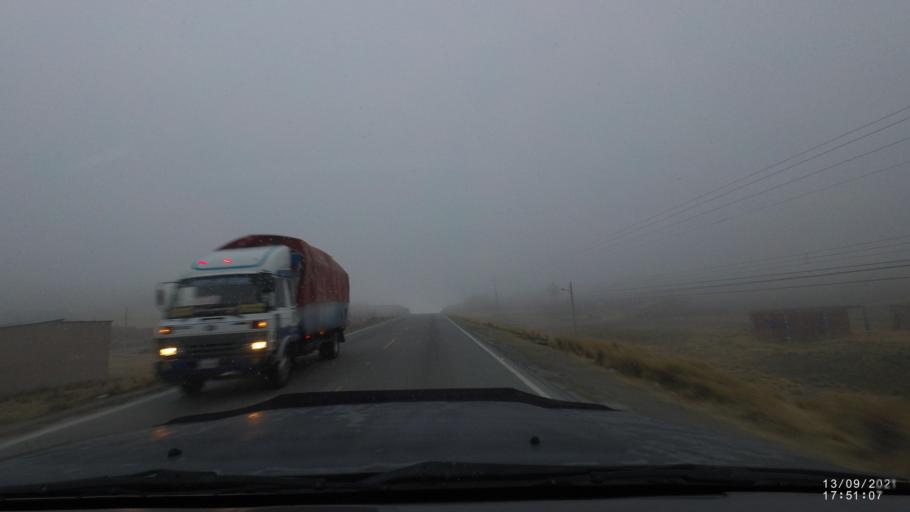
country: BO
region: Cochabamba
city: Colomi
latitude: -17.3980
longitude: -65.8666
